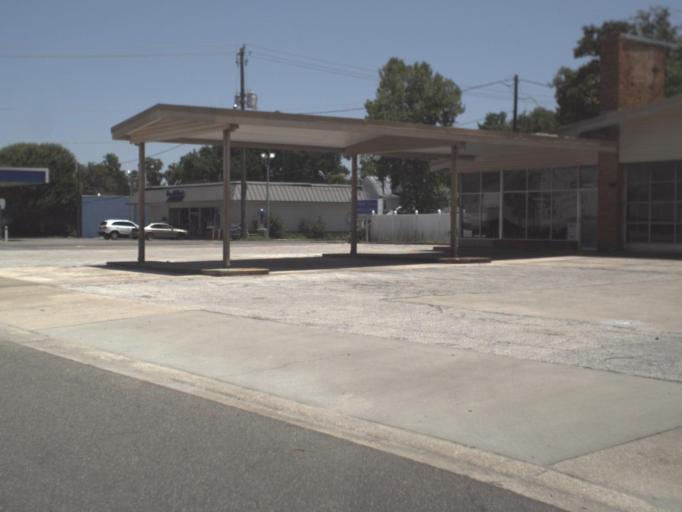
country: US
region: Florida
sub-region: Columbia County
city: Lake City
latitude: 30.1893
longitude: -82.6385
